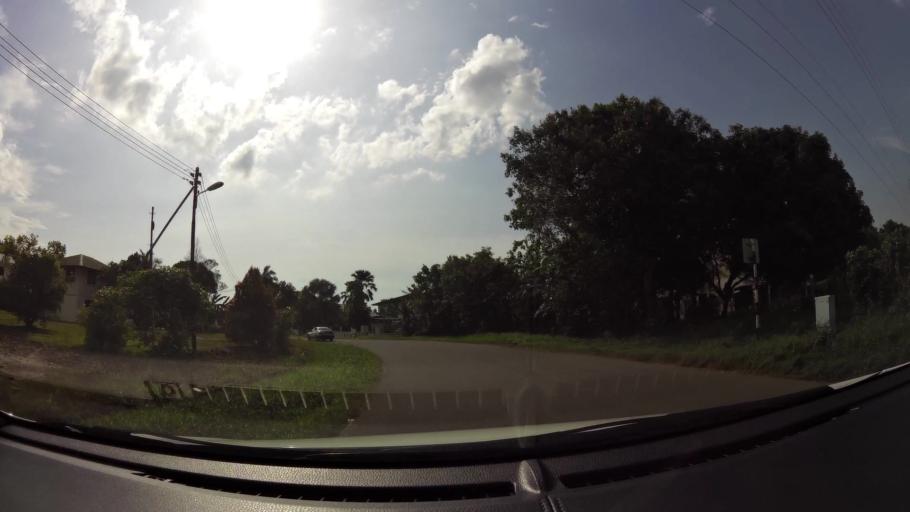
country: BN
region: Brunei and Muara
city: Bandar Seri Begawan
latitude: 4.9572
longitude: 114.9705
